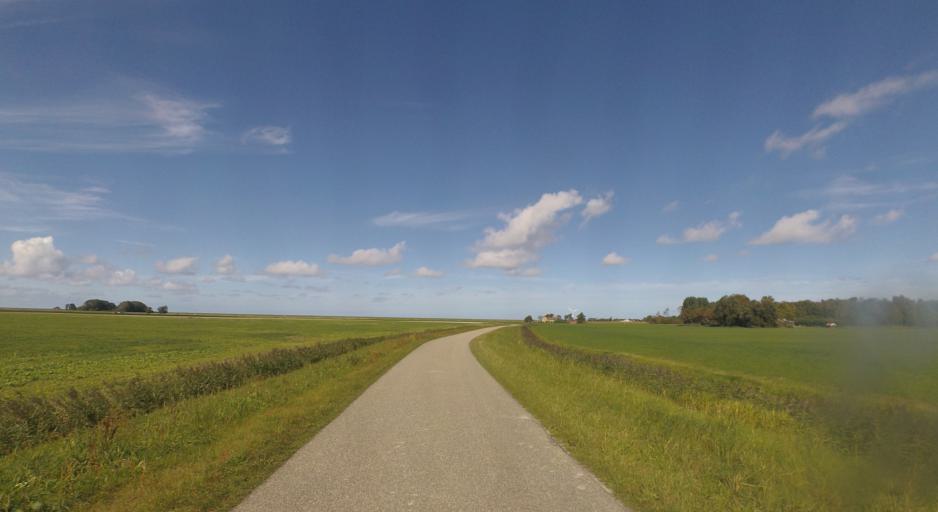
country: NL
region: Friesland
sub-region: Gemeente Dongeradeel
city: Holwerd
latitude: 53.3617
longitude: 5.8962
